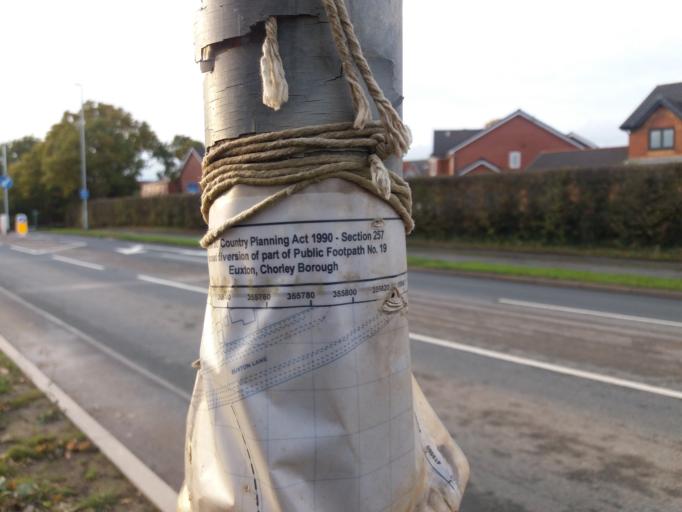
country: GB
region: England
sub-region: Lancashire
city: Euxton
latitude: 53.6713
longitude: -2.6716
